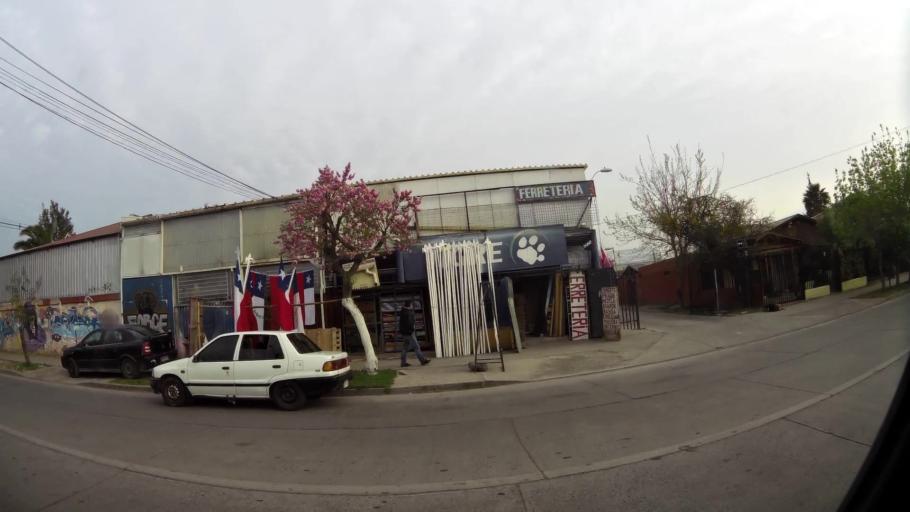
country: CL
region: Santiago Metropolitan
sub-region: Provincia de Santiago
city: Lo Prado
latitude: -33.5222
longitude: -70.7921
